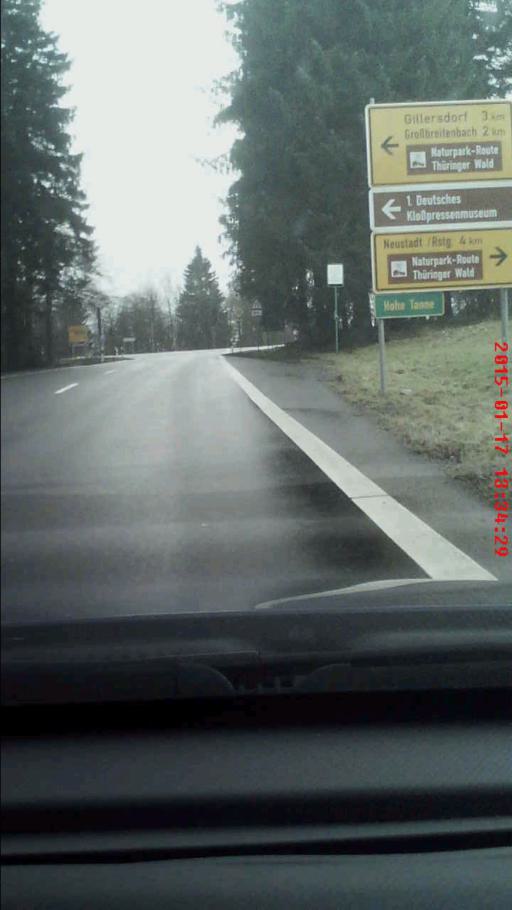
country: DE
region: Thuringia
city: Grossbreitenbach
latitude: 50.5965
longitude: 10.9839
